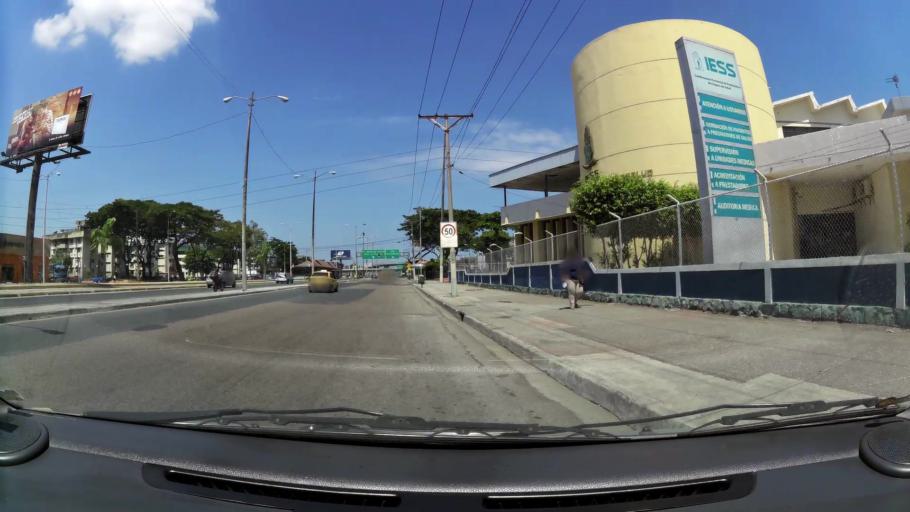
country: EC
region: Guayas
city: Guayaquil
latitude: -2.2353
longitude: -79.8971
